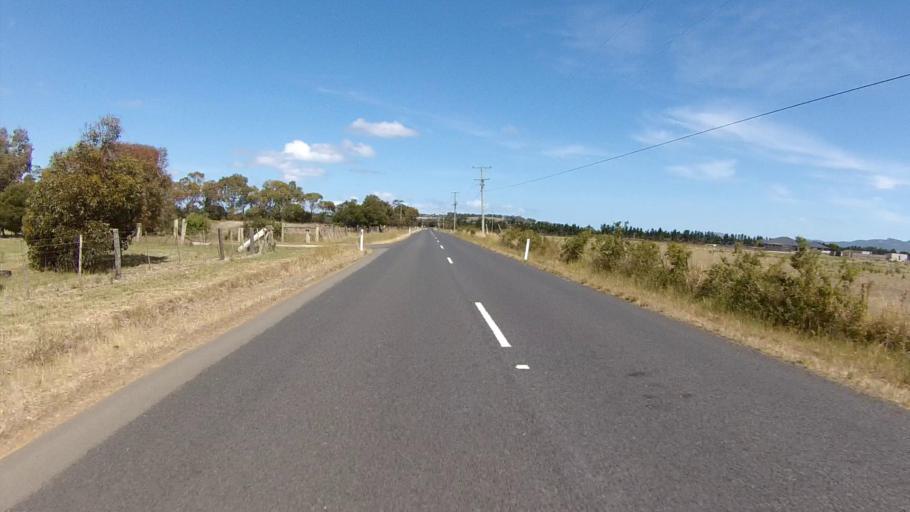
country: AU
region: Tasmania
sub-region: Sorell
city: Sorell
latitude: -42.7742
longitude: 147.5192
